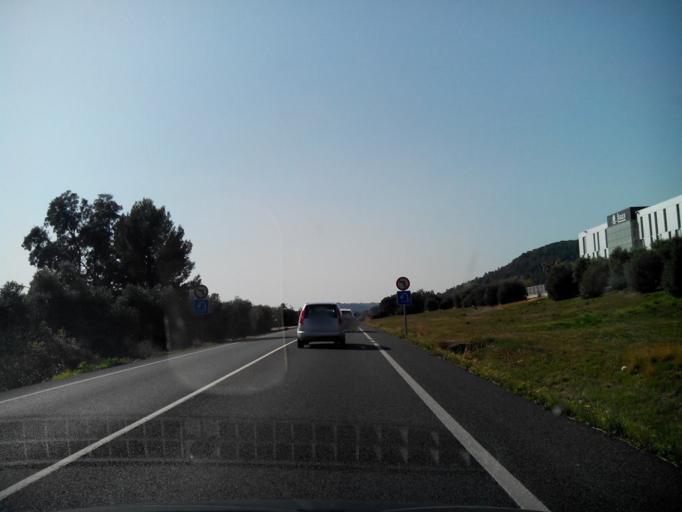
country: ES
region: Catalonia
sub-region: Provincia de Tarragona
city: Alcover
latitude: 41.2776
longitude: 1.1804
